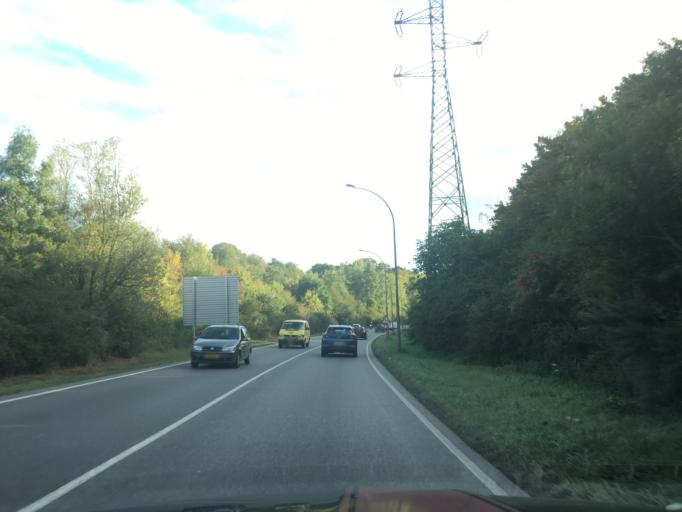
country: LU
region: Luxembourg
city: Soleuvre
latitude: 49.5314
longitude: 5.9278
